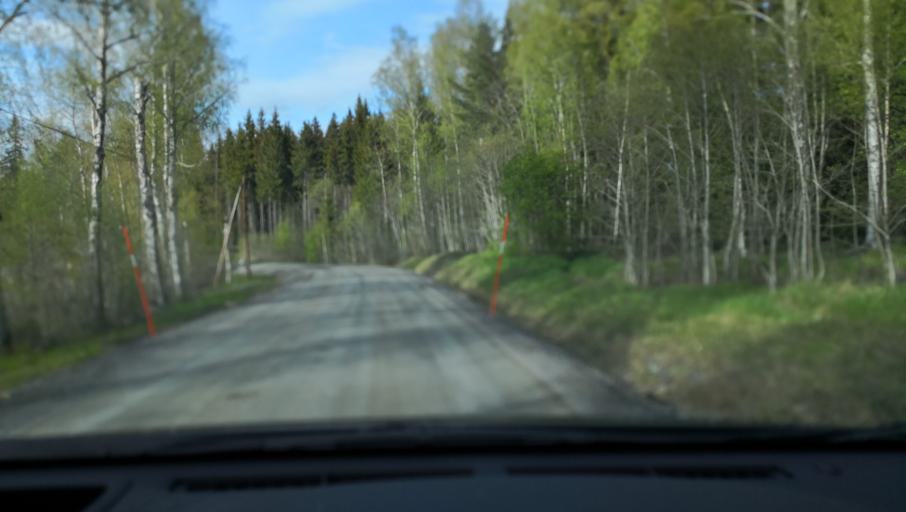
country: SE
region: Dalarna
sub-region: Saters Kommun
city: Saeter
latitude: 60.2736
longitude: 15.8359
